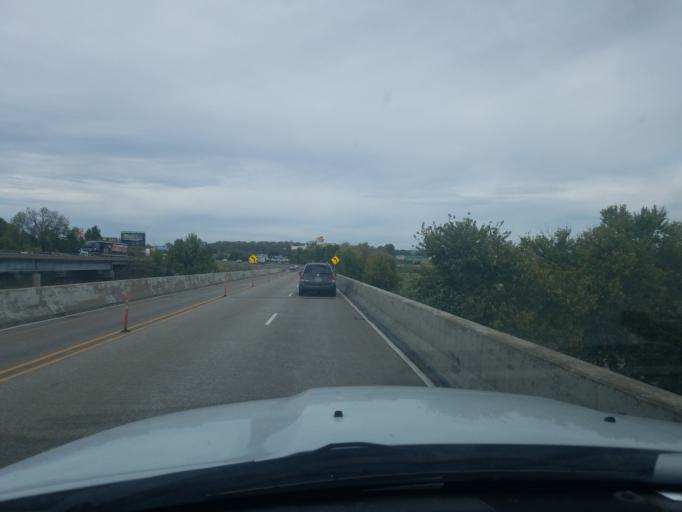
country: US
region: Indiana
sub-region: Vanderburgh County
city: Evansville
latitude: 37.9106
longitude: -87.5482
